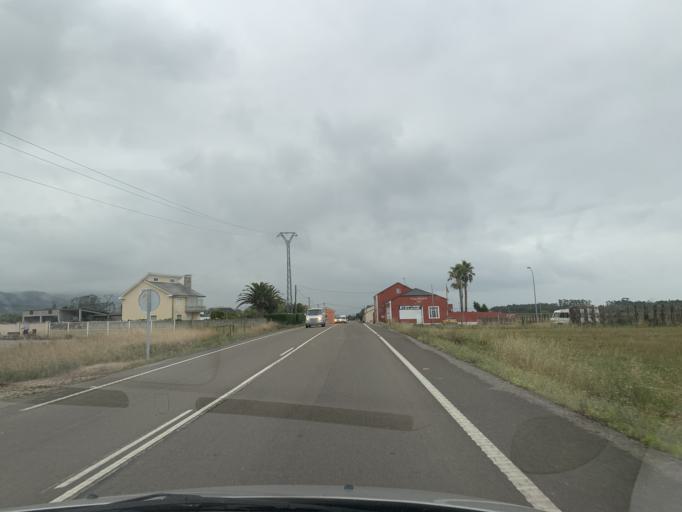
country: ES
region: Galicia
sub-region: Provincia de Lugo
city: Ribadeo
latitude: 43.5457
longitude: -7.0889
